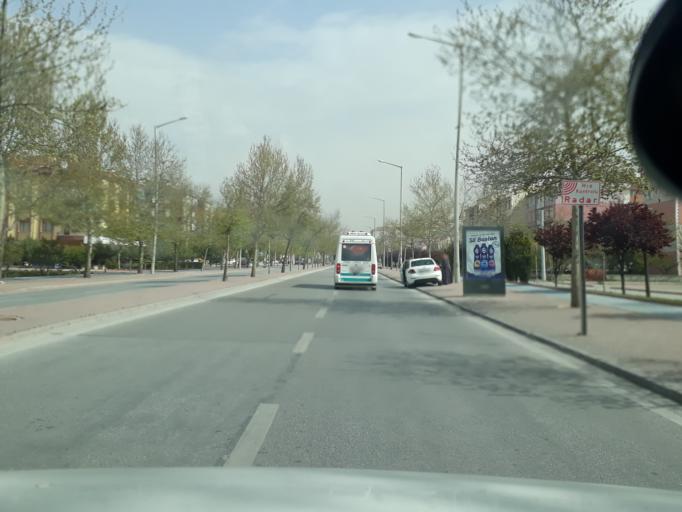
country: TR
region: Konya
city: Selcuklu
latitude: 37.9379
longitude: 32.4931
